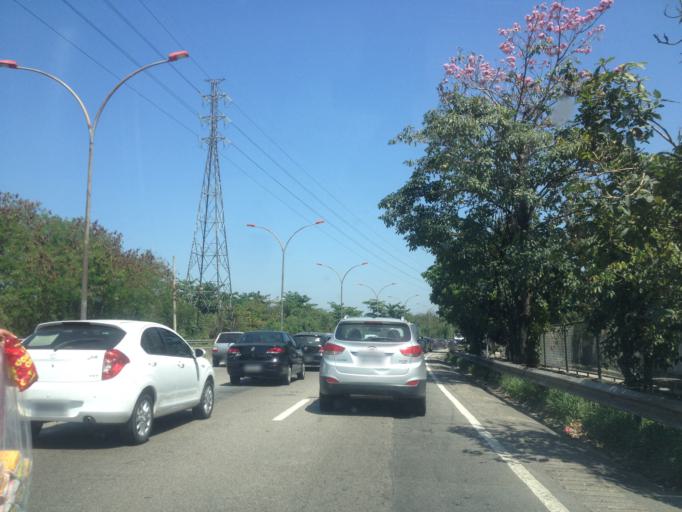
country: BR
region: Rio de Janeiro
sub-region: Duque De Caxias
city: Duque de Caxias
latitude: -22.8005
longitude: -43.3212
